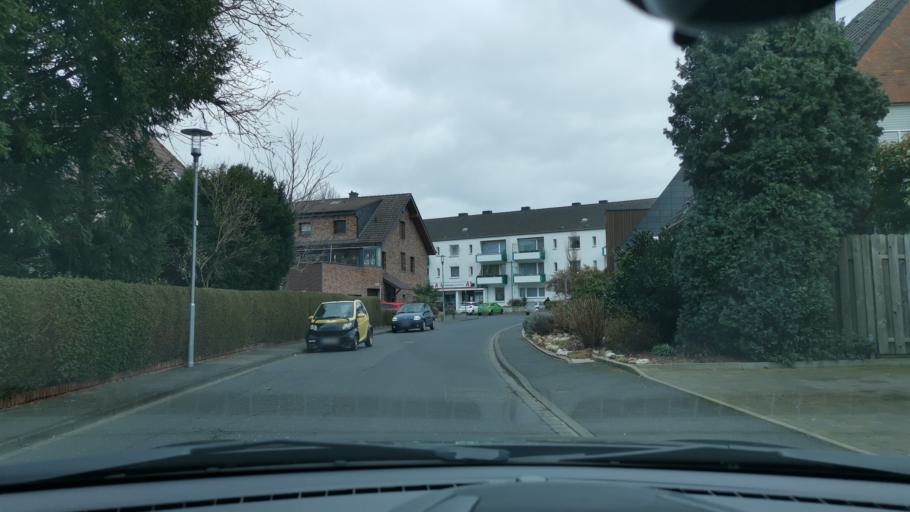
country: DE
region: North Rhine-Westphalia
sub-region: Regierungsbezirk Dusseldorf
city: Grevenbroich
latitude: 51.0835
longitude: 6.5998
